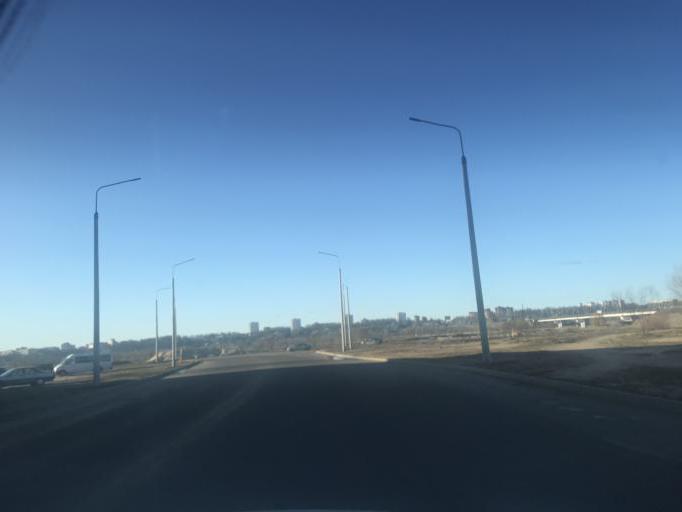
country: BY
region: Mogilev
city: Mahilyow
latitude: 53.8846
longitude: 30.3753
